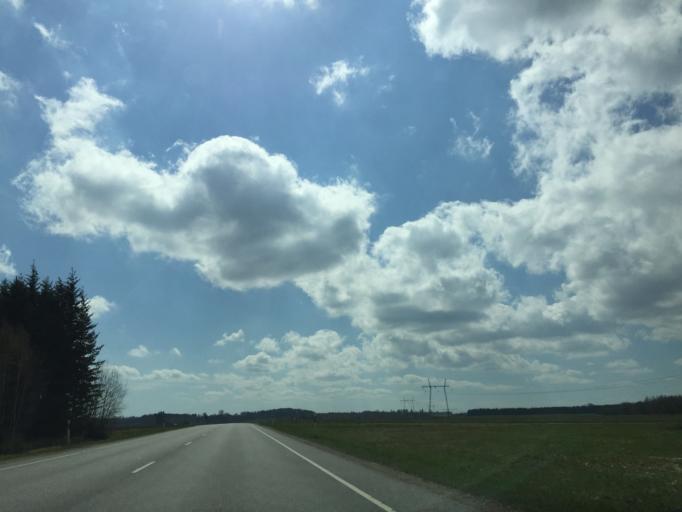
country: EE
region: Tartu
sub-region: Elva linn
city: Elva
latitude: 58.2049
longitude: 26.3578
